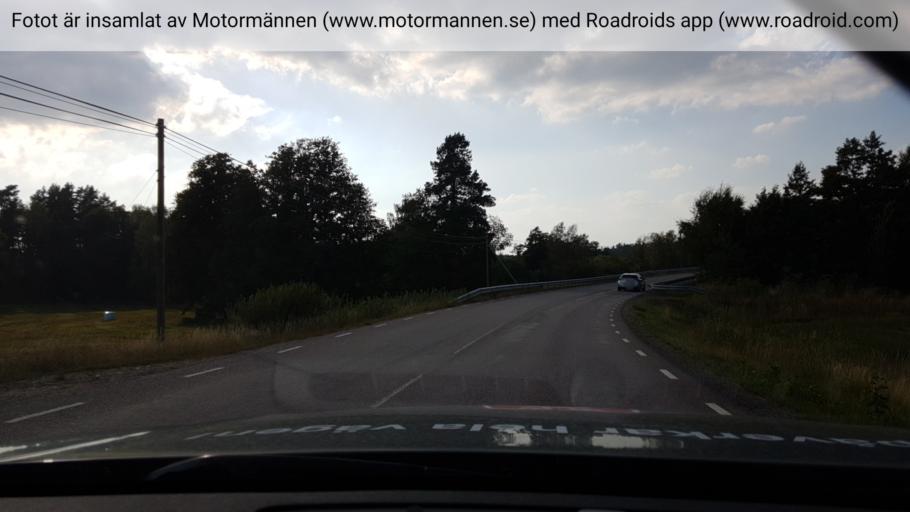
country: SE
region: Soedermanland
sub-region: Gnesta Kommun
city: Gnesta
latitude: 59.0722
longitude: 17.2886
